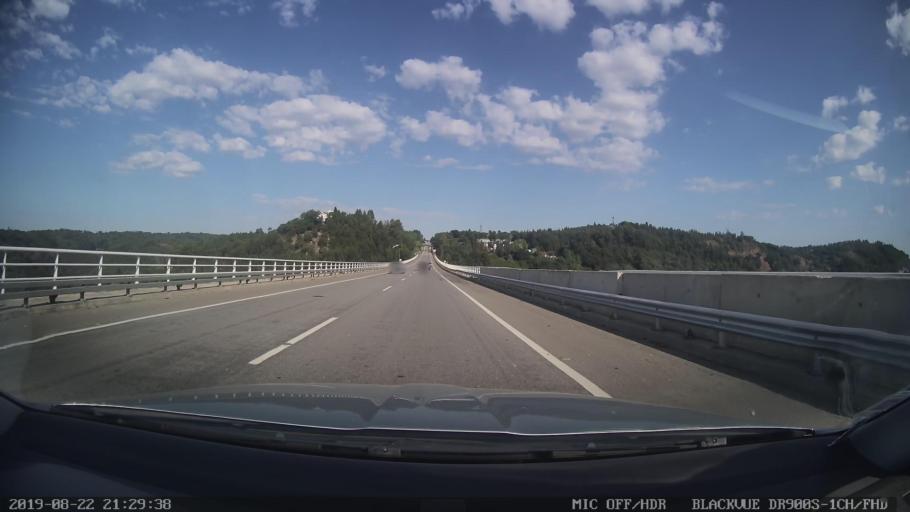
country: PT
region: Leiria
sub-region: Pedrogao Grande
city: Pedrogao Grande
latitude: 39.9039
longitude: -8.1384
